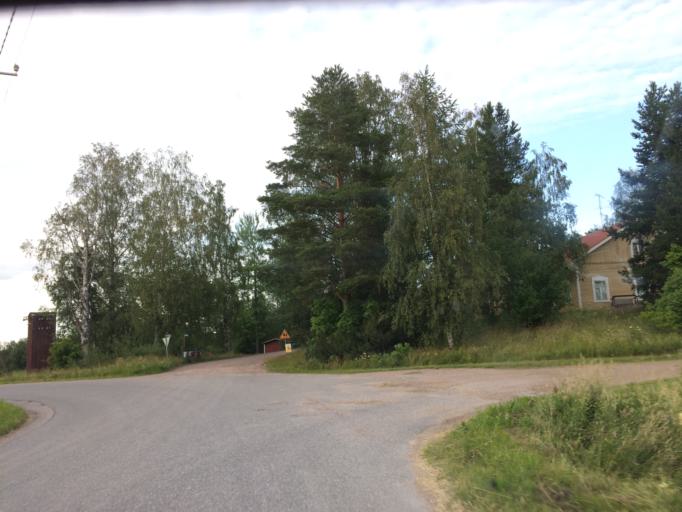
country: FI
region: Haeme
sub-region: Haemeenlinna
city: Tervakoski
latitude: 60.8358
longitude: 24.6279
